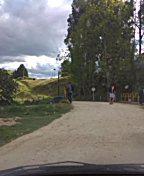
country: CO
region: Boyaca
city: Duitama
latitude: 5.8256
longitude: -73.0791
